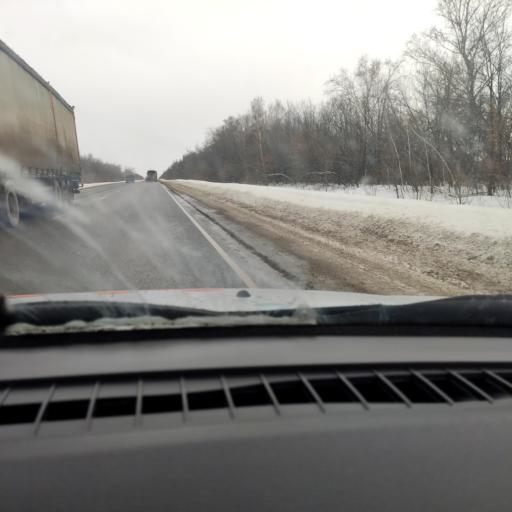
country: RU
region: Samara
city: Dubovyy Umet
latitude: 52.9947
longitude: 50.2573
